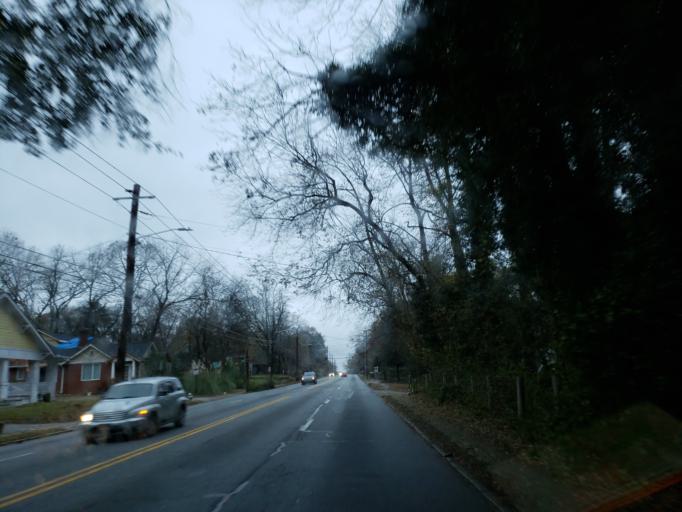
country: US
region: Georgia
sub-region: DeKalb County
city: Gresham Park
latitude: 33.7259
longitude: -84.3494
